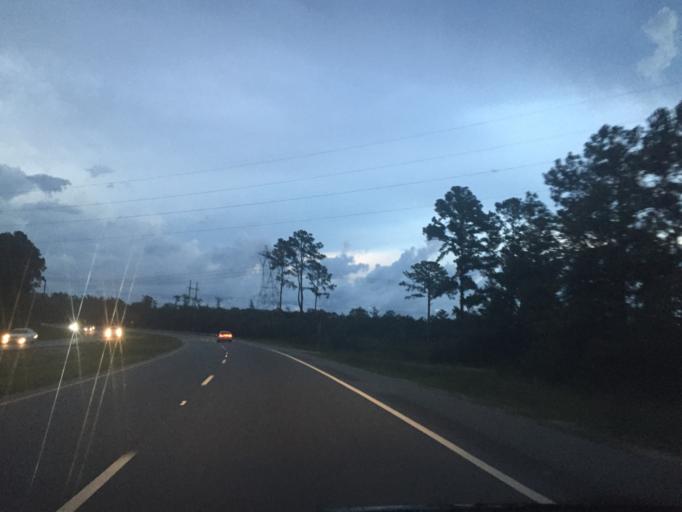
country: US
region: Georgia
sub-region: Liberty County
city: Midway
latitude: 31.8276
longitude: -81.4929
